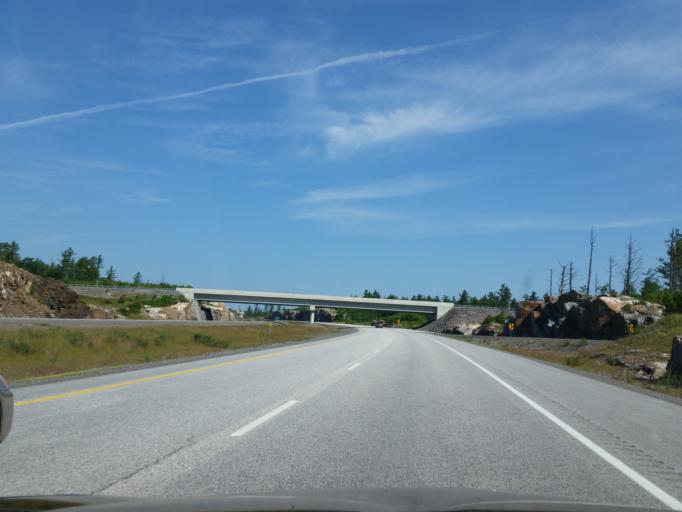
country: CA
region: Ontario
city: Greater Sudbury
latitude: 46.2269
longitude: -80.7713
